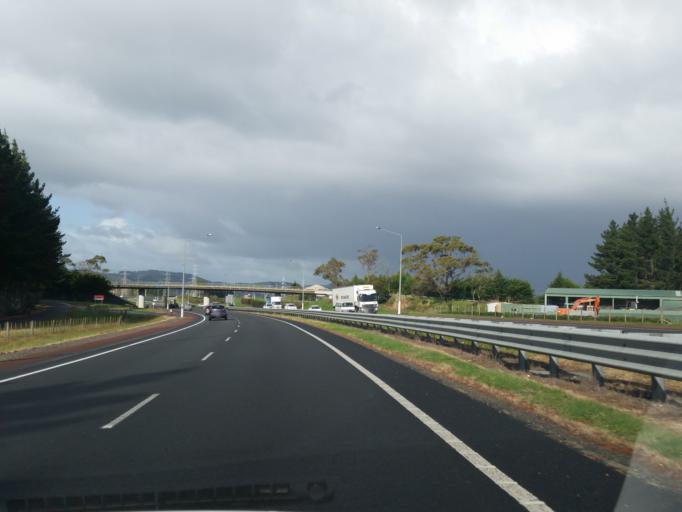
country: NZ
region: Auckland
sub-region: Auckland
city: Papakura
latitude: -37.1164
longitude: 174.9500
